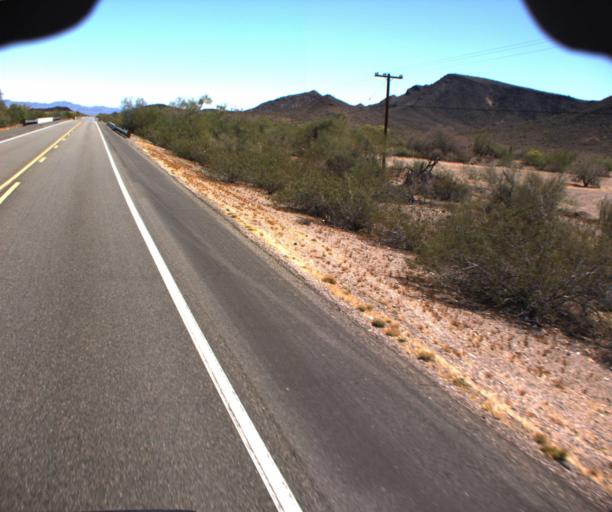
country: US
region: Arizona
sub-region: La Paz County
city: Quartzsite
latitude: 33.6802
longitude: -113.9425
